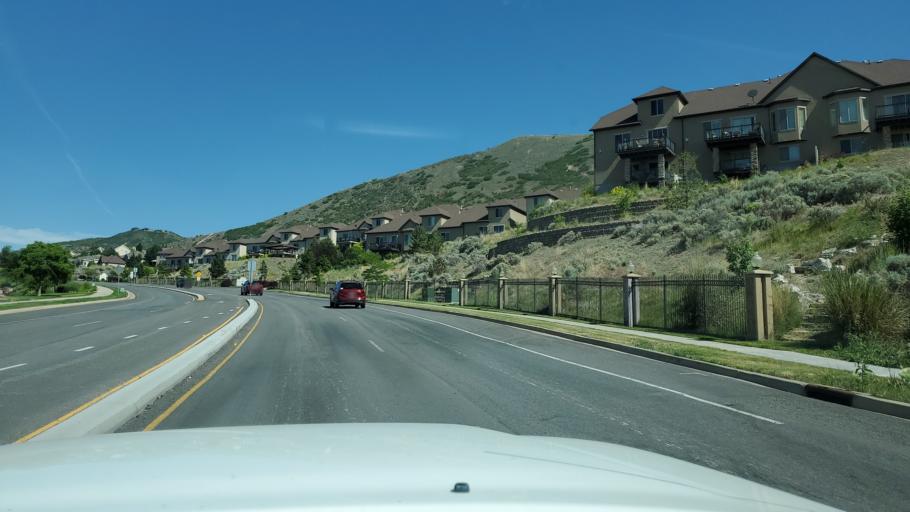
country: US
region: Utah
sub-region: Salt Lake County
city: Draper
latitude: 40.4846
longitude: -111.8832
